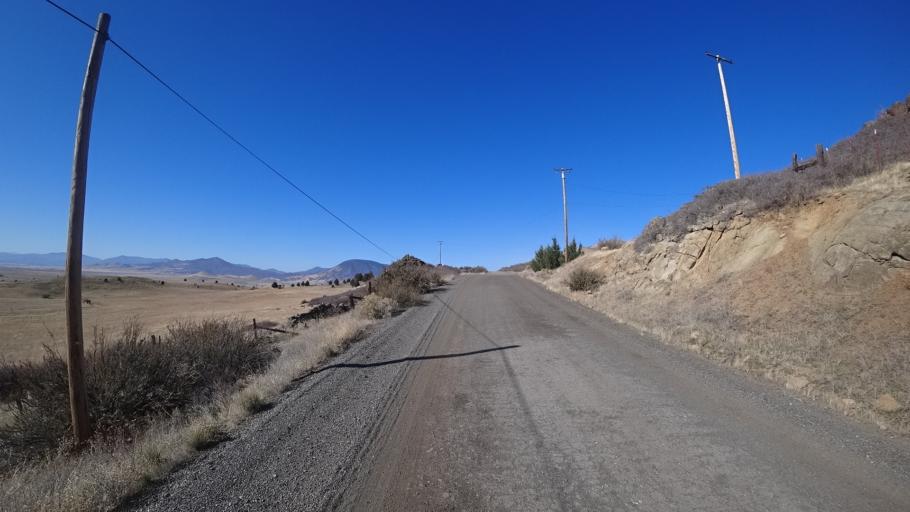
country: US
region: California
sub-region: Siskiyou County
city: Montague
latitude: 41.8311
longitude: -122.3718
